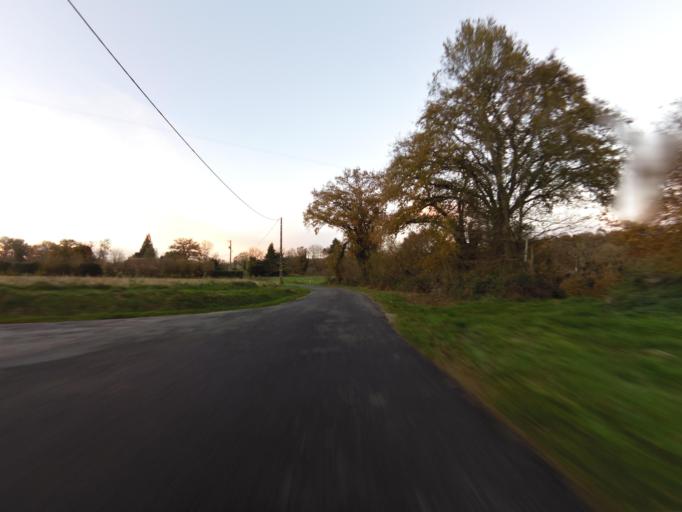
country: FR
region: Brittany
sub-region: Departement du Morbihan
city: Pluherlin
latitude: 47.7166
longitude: -2.3628
